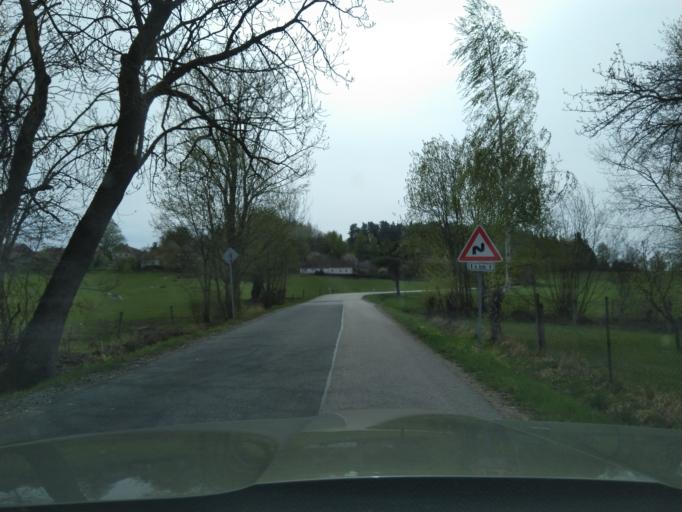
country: CZ
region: Jihocesky
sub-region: Okres Prachatice
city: Stachy
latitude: 49.1834
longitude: 13.6469
